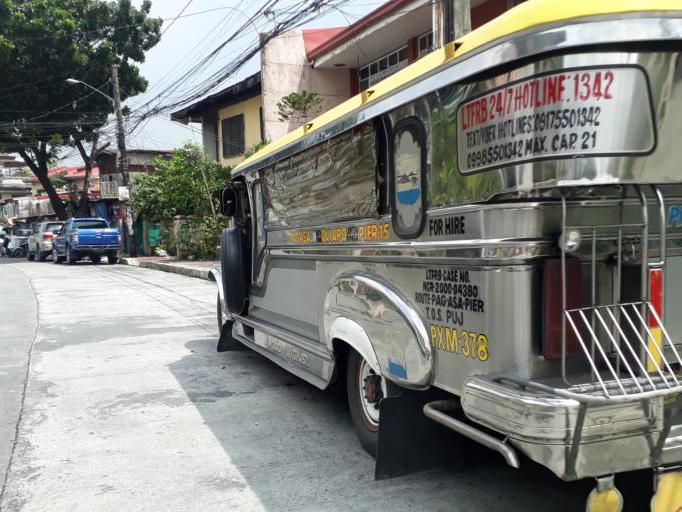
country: PH
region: Calabarzon
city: Bagong Pagasa
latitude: 14.6639
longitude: 121.0346
